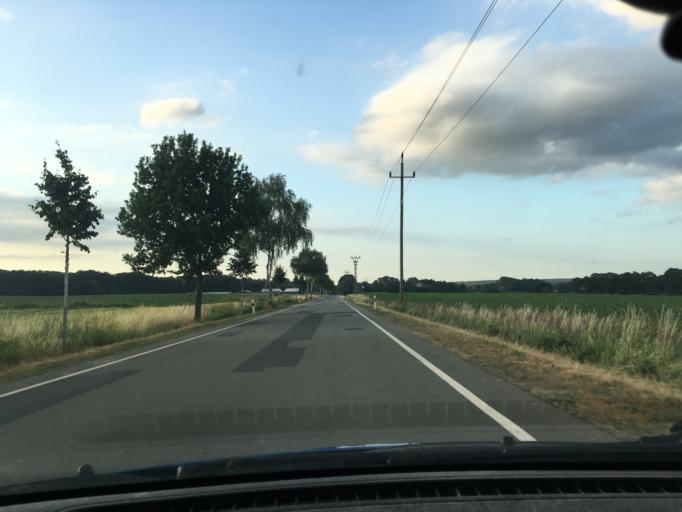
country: DE
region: Lower Saxony
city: Eyendorf
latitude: 53.1862
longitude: 10.1865
